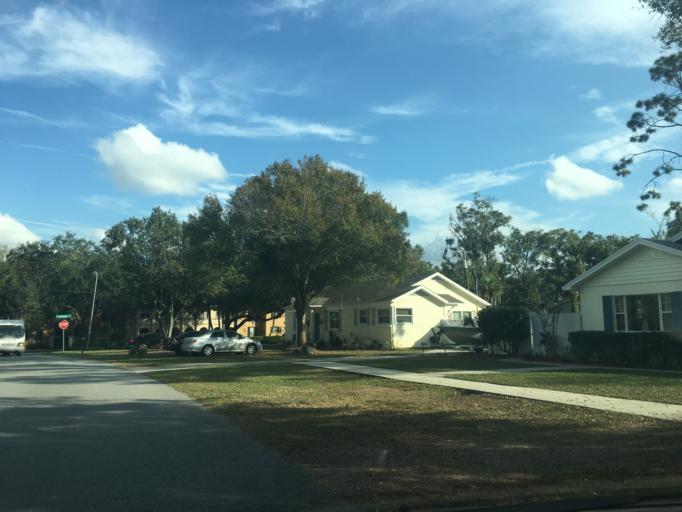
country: US
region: Florida
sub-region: Hillsborough County
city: Egypt Lake-Leto
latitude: 27.9943
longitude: -82.4687
